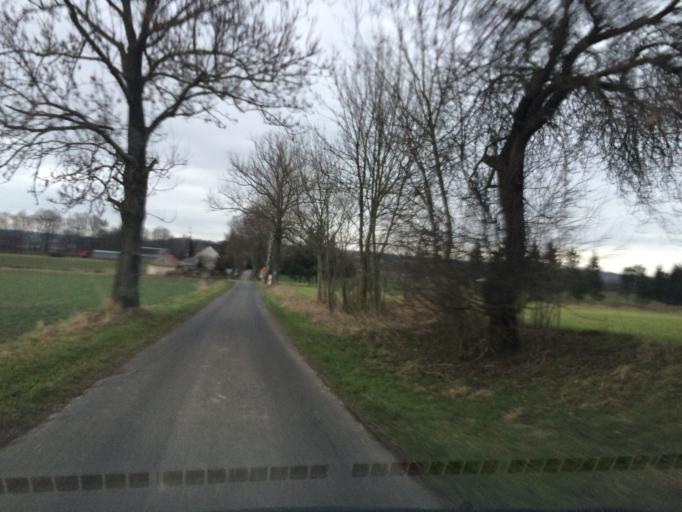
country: PL
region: Lower Silesian Voivodeship
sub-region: Powiat lubanski
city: Luban
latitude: 51.1487
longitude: 15.3022
